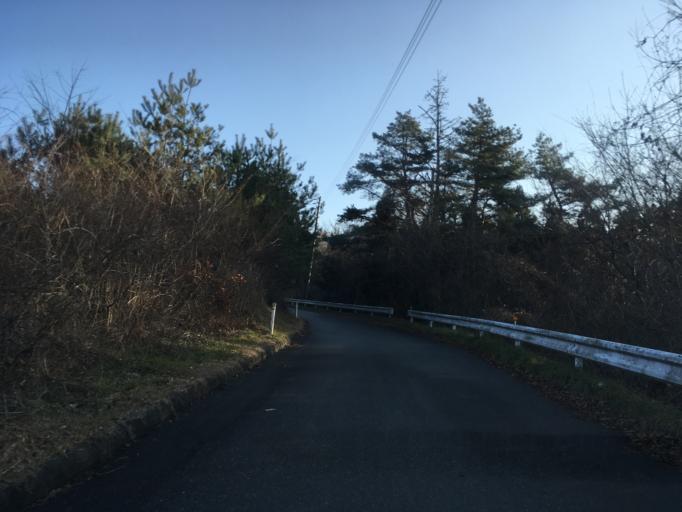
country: JP
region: Iwate
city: Ichinoseki
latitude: 38.8237
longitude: 141.2623
